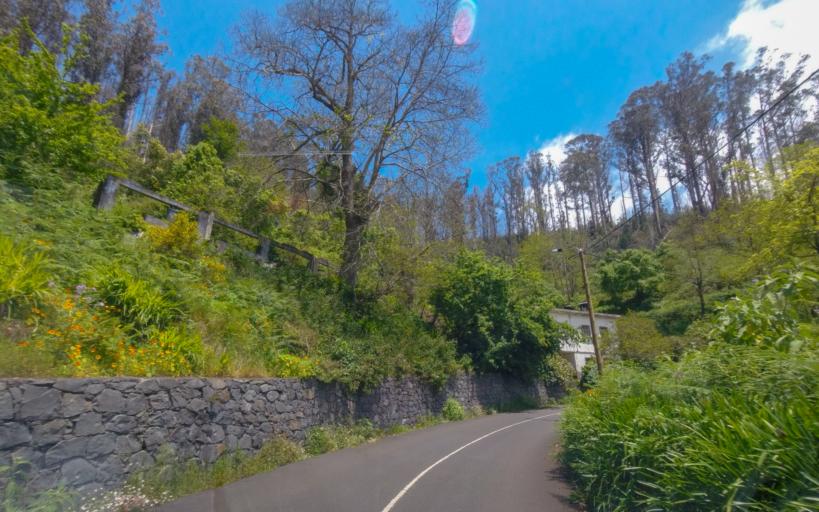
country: PT
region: Madeira
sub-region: Funchal
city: Nossa Senhora do Monte
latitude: 32.6826
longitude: -16.8839
